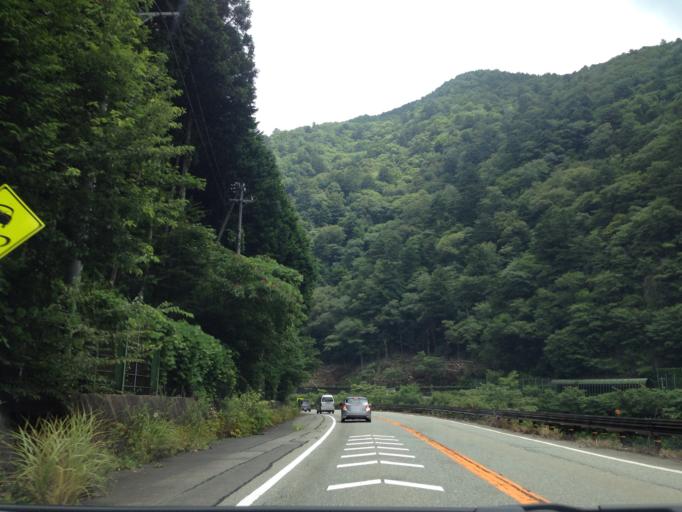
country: JP
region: Gifu
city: Gujo
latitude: 35.7545
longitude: 137.2282
